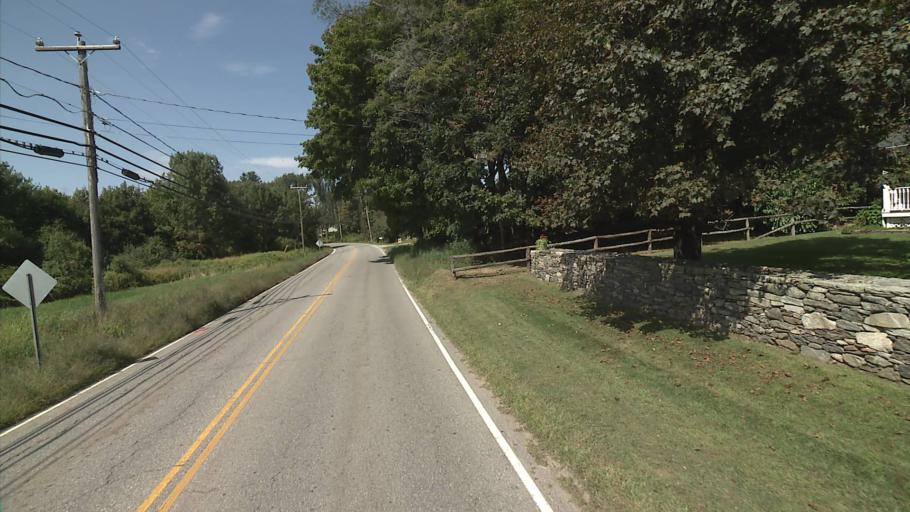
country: US
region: Connecticut
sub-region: Windham County
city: South Windham
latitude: 41.6276
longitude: -72.1992
